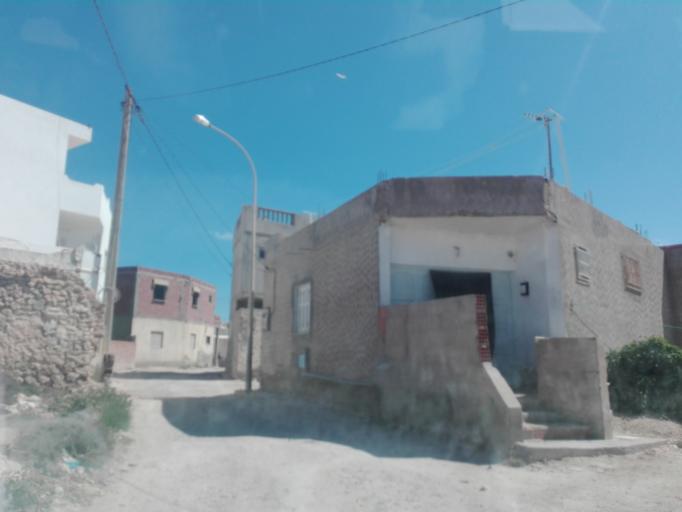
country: TN
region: Safaqis
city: Jabinyanah
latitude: 34.7448
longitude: 11.2935
